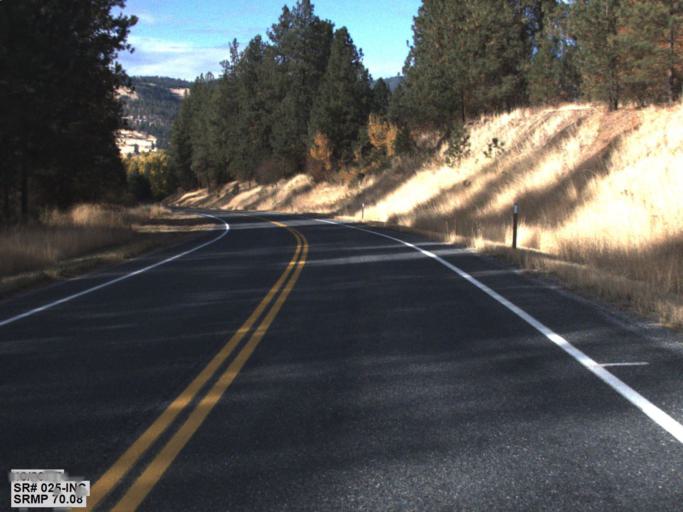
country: US
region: Washington
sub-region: Stevens County
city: Kettle Falls
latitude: 48.4783
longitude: -118.1697
